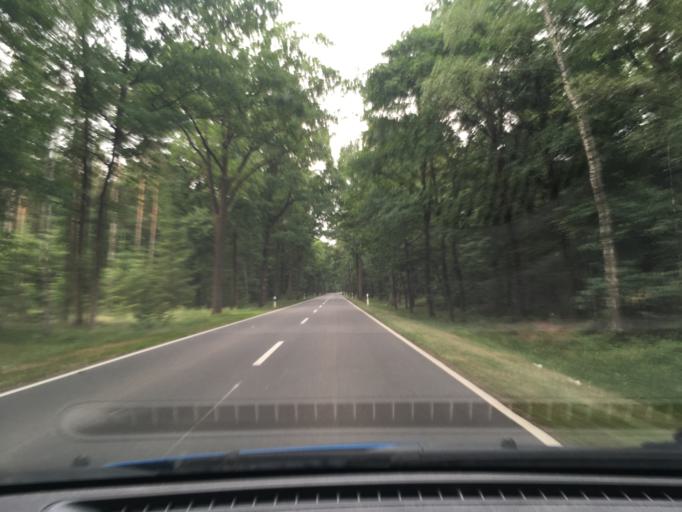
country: DE
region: Lower Saxony
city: Walsrode
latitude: 52.8163
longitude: 9.6009
